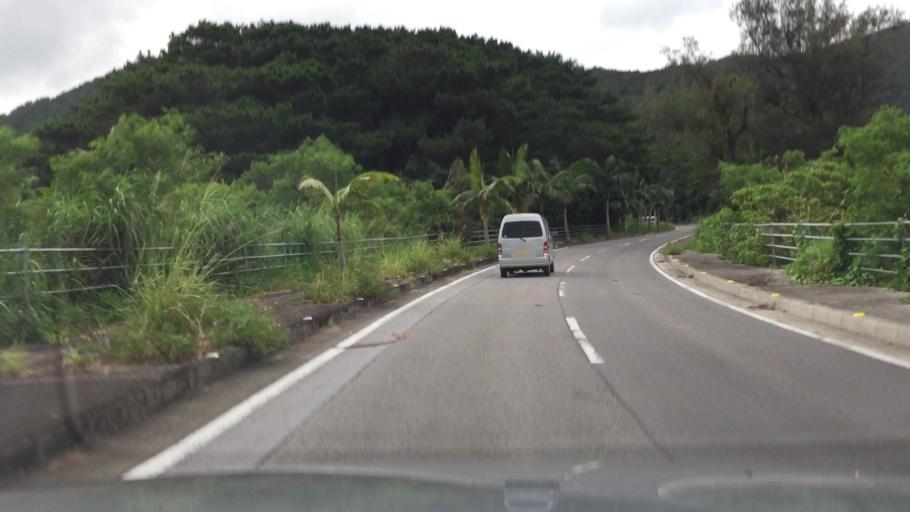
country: JP
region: Okinawa
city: Ishigaki
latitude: 24.4469
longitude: 124.1337
